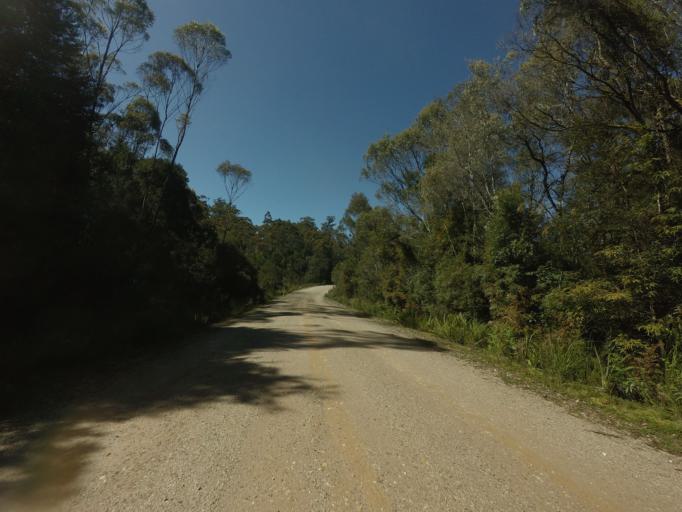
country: AU
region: Tasmania
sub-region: Huon Valley
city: Geeveston
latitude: -42.9871
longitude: 146.3686
